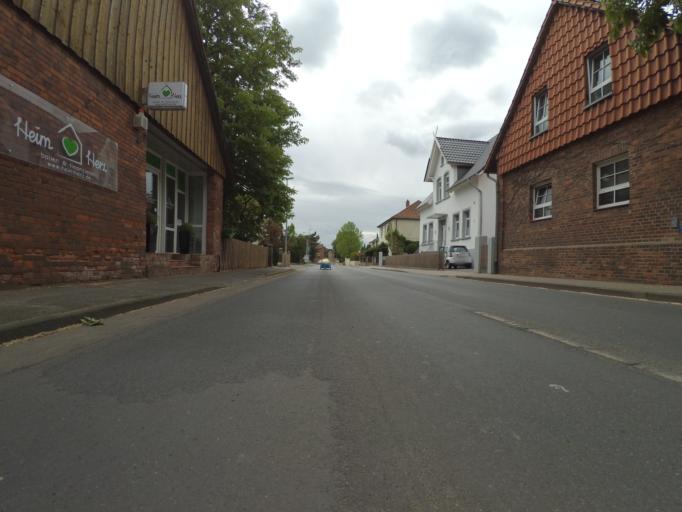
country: DE
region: Lower Saxony
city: Isernhagen Farster Bauerschaft
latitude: 52.4549
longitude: 9.7960
